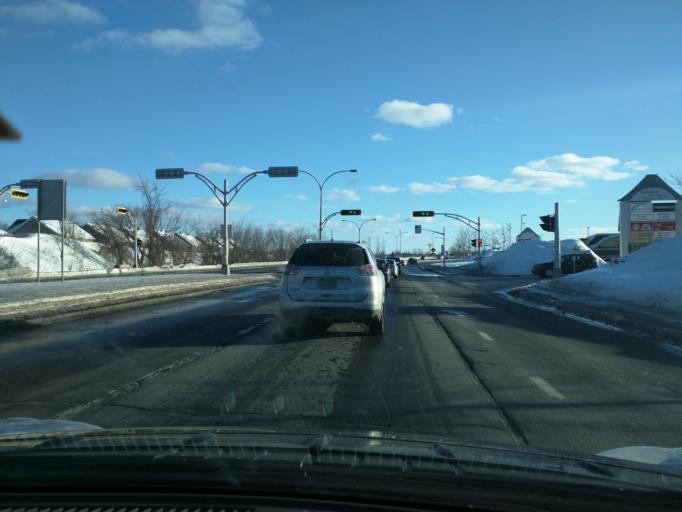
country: CA
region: Quebec
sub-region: Laurentides
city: Rosemere
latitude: 45.5896
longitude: -73.7863
